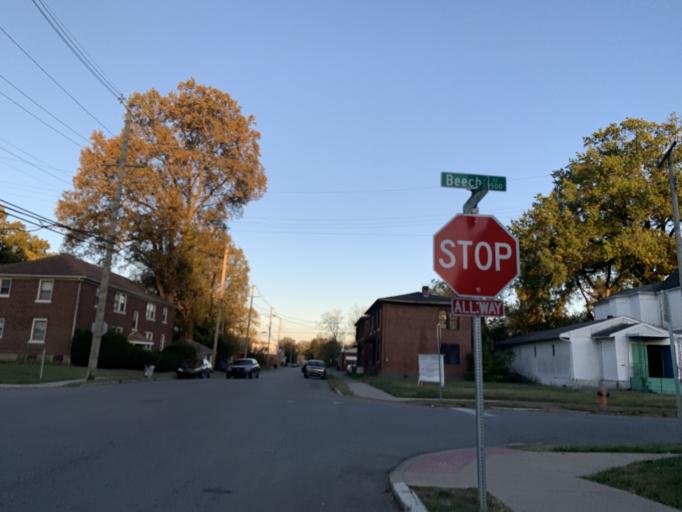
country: US
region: Kentucky
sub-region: Jefferson County
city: Shively
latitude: 38.2320
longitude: -85.8054
